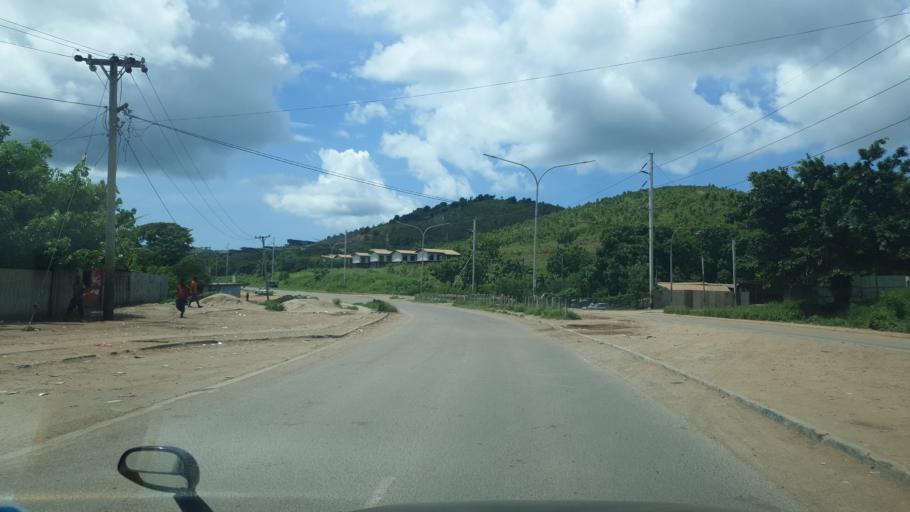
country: PG
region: National Capital
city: Port Moresby
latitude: -9.3888
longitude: 147.1535
